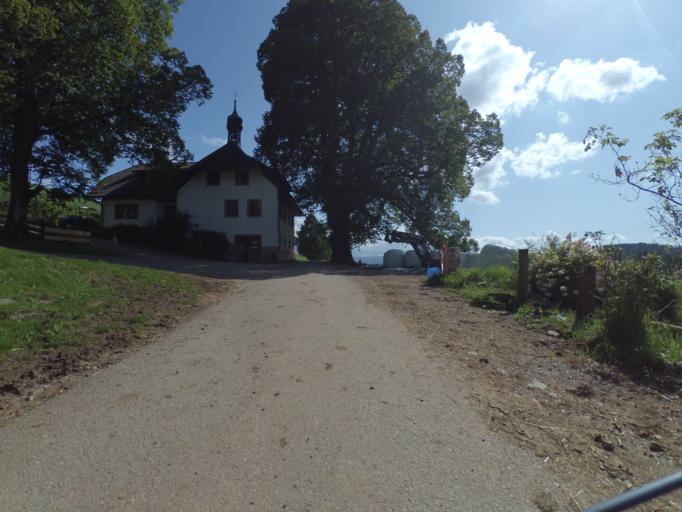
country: DE
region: Baden-Wuerttemberg
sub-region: Freiburg Region
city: Sankt Peter
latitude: 48.0326
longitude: 8.0276
